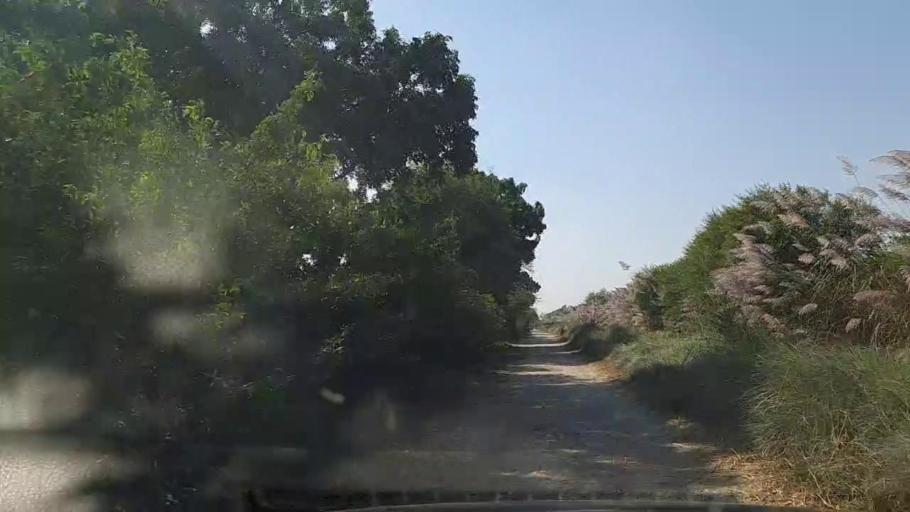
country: PK
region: Sindh
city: Daro Mehar
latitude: 24.8378
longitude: 68.1157
